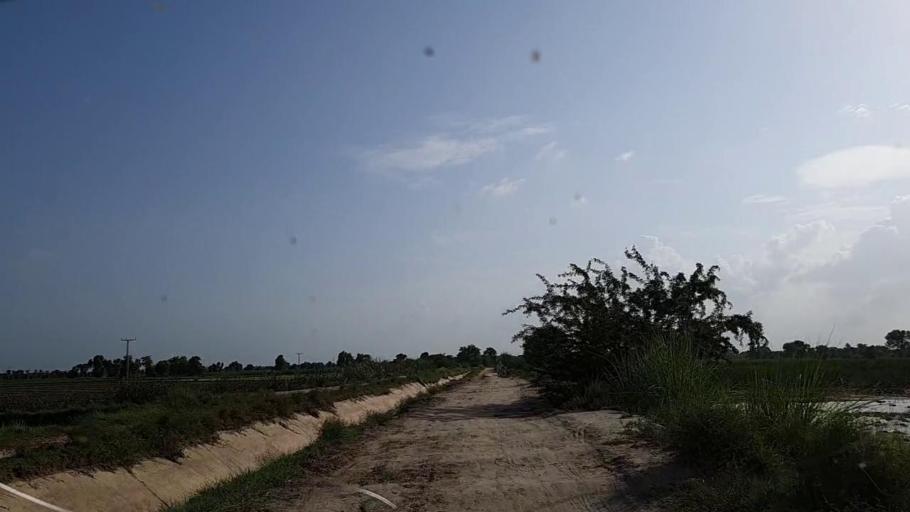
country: PK
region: Sindh
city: Bhiria
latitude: 26.8661
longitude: 68.2549
